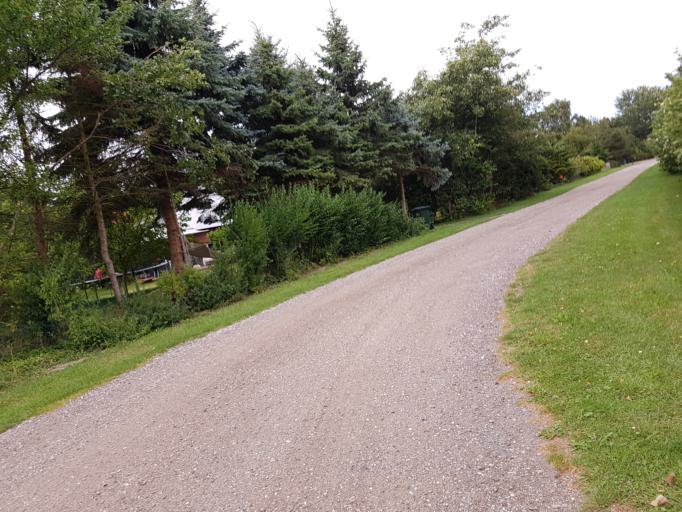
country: DK
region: Zealand
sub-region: Guldborgsund Kommune
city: Nykobing Falster
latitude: 54.5921
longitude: 11.9608
